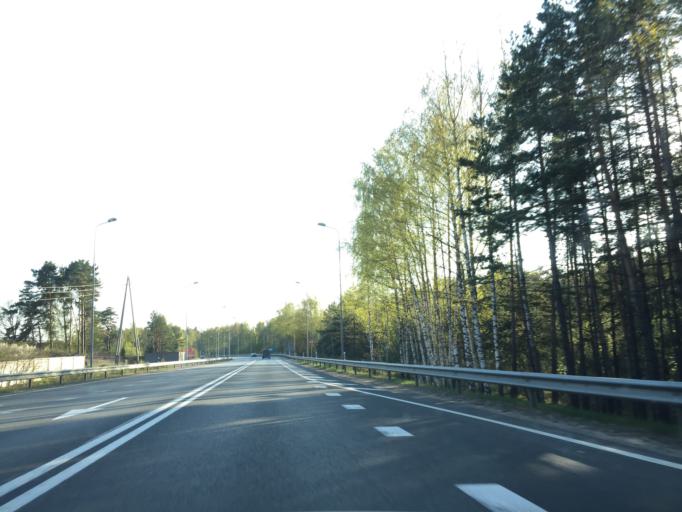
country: LV
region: Saulkrastu
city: Saulkrasti
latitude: 57.1916
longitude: 24.3524
